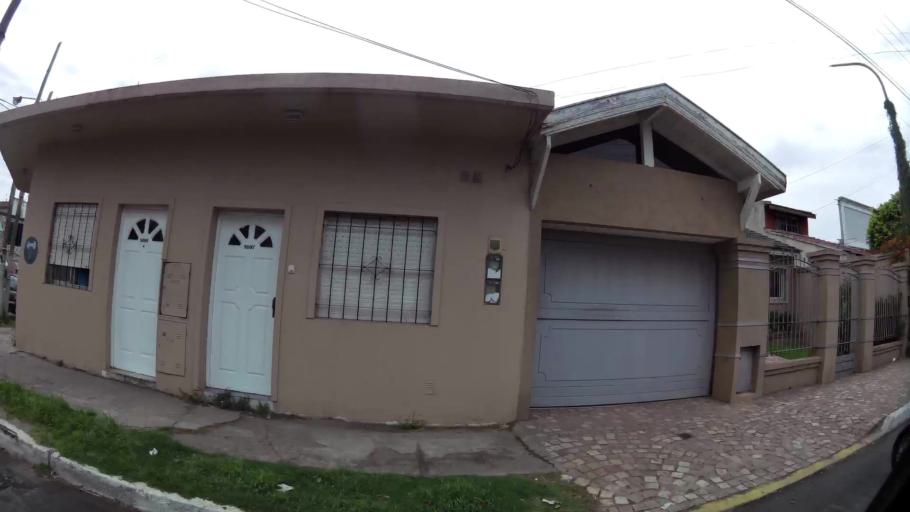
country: AR
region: Buenos Aires
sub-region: Partido de Quilmes
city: Quilmes
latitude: -34.7508
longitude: -58.2126
